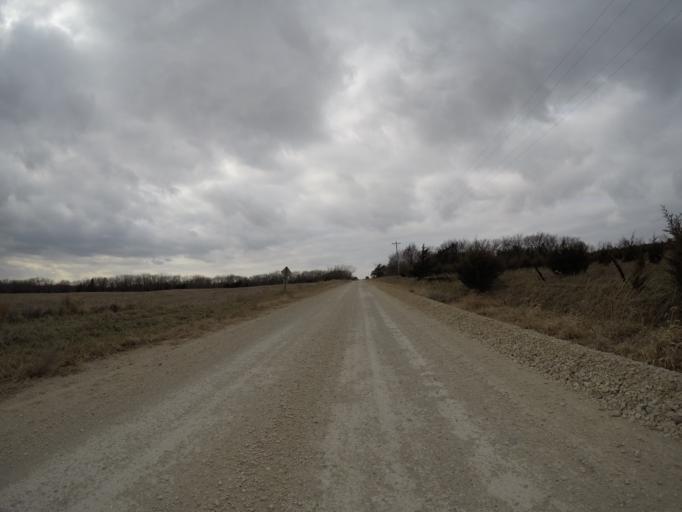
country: US
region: Kansas
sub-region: Morris County
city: Council Grove
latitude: 38.7679
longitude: -96.2843
